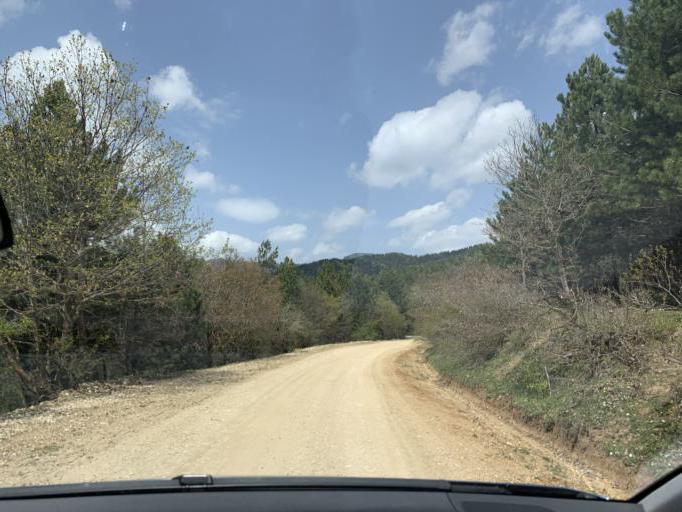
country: TR
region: Bolu
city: Bolu
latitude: 40.8309
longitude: 31.6742
